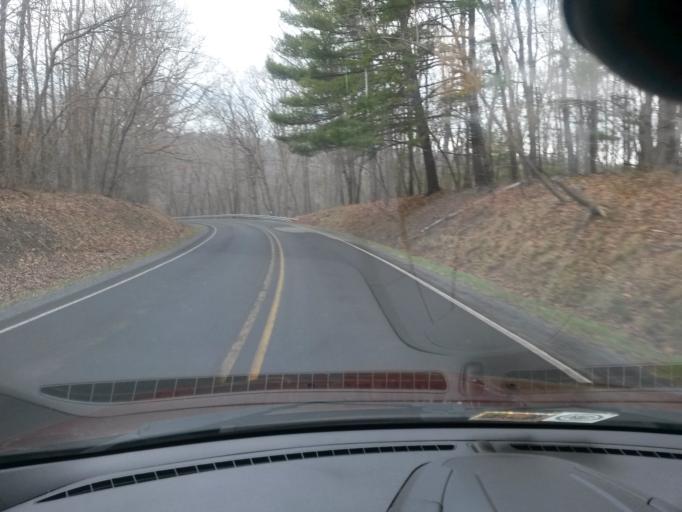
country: US
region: Virginia
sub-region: Bath County
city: Warm Springs
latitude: 38.0829
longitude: -79.7845
